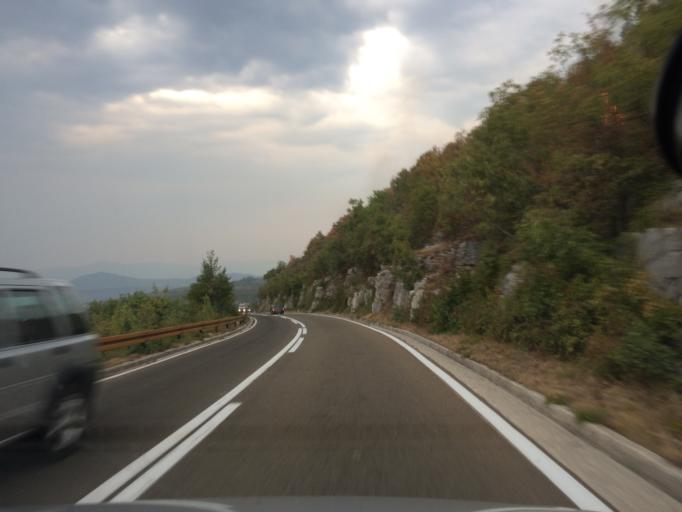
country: ME
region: Opstina Niksic
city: Niksic
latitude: 42.8730
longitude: 18.9374
